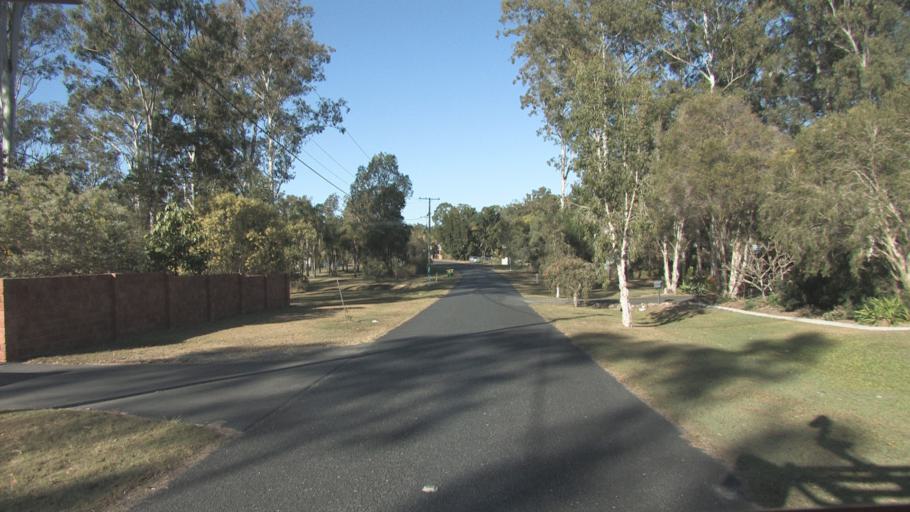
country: AU
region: Queensland
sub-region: Logan
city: North Maclean
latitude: -27.7459
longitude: 153.0096
